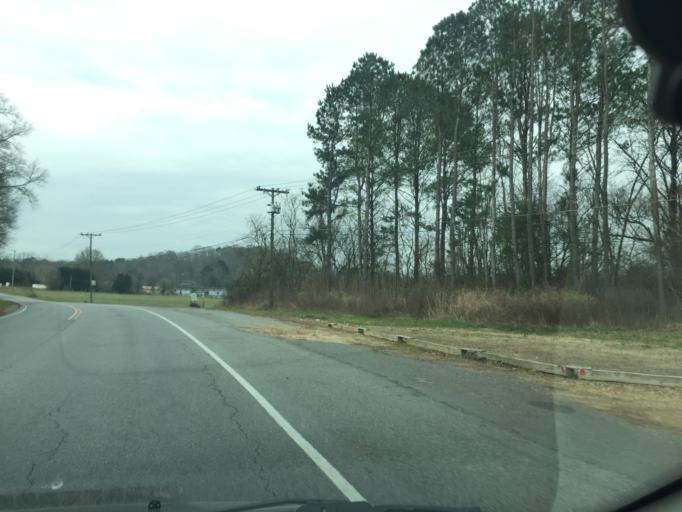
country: US
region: Tennessee
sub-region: Hamilton County
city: East Brainerd
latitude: 34.9771
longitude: -85.1457
